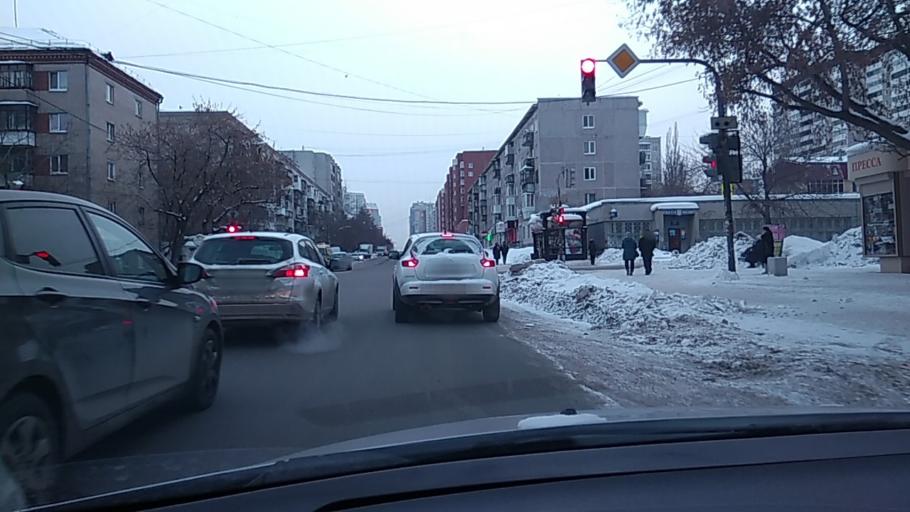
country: RU
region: Sverdlovsk
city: Yekaterinburg
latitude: 56.8129
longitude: 60.5997
